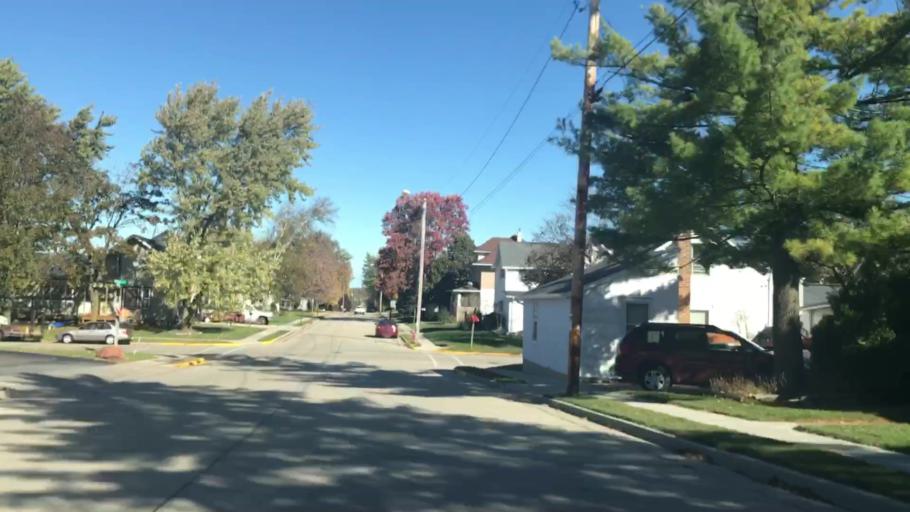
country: US
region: Wisconsin
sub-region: Dodge County
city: Mayville
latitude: 43.4952
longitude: -88.5524
